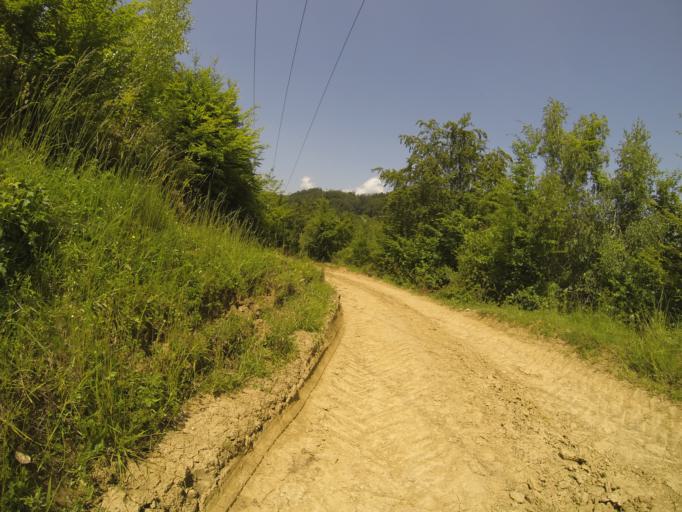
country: RO
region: Valcea
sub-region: Oras Baile Olanesti
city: Baile Olanesti
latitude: 45.2058
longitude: 24.2115
